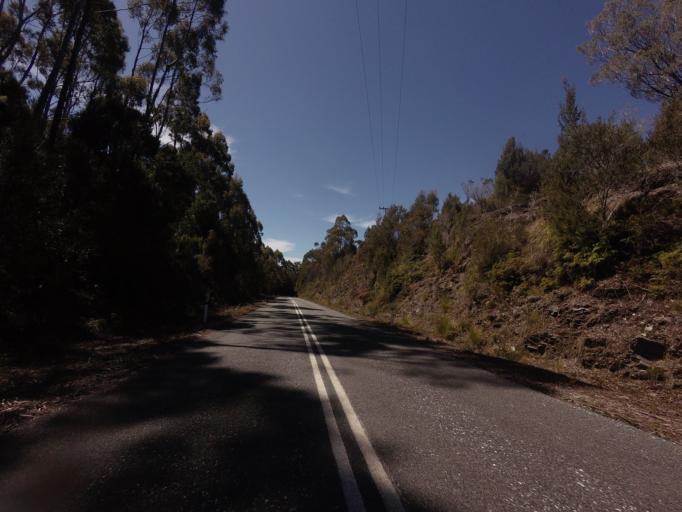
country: AU
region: Tasmania
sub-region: West Coast
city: Queenstown
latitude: -42.7677
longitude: 146.0178
